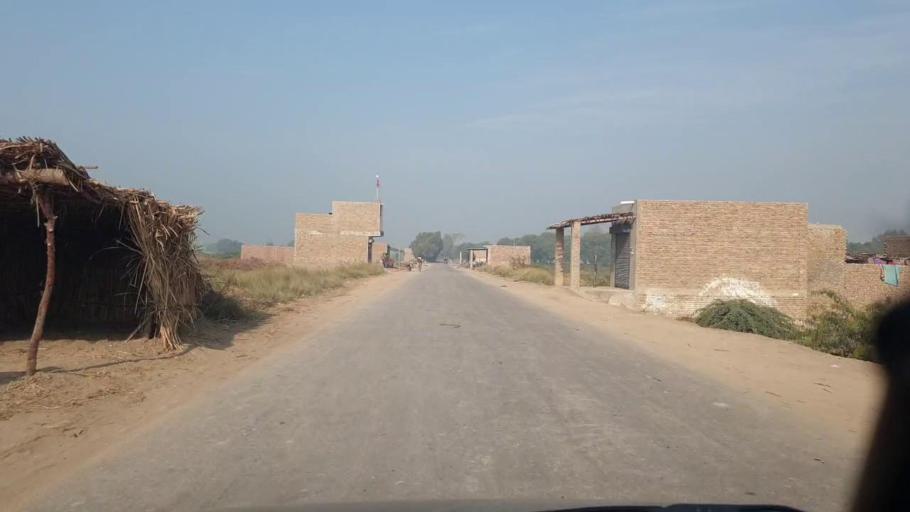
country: PK
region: Sindh
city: Shahdadpur
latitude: 25.9342
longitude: 68.6093
